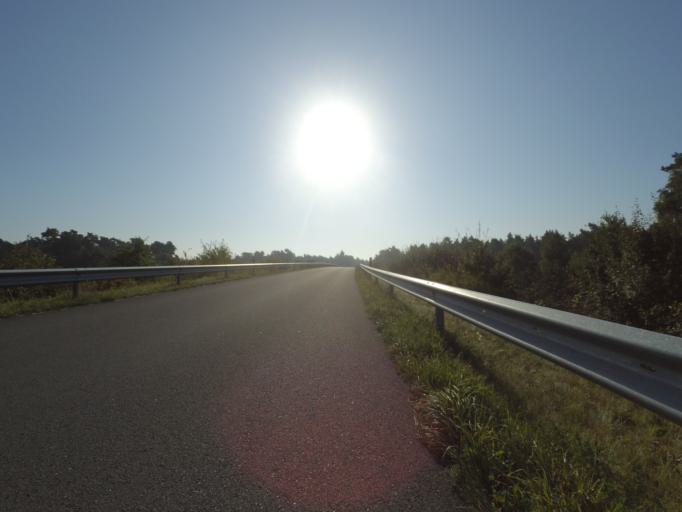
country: DE
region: Lower Saxony
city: Suddendorf
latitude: 52.2842
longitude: 7.2075
